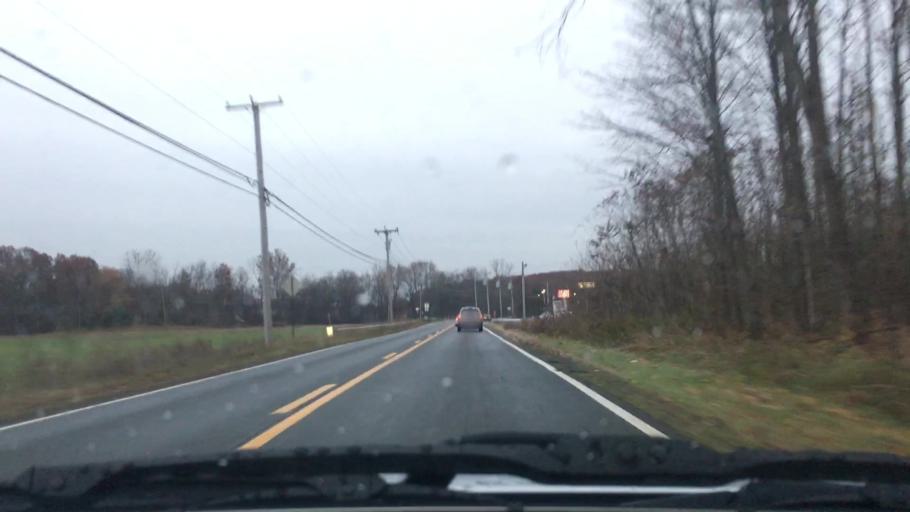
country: US
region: Massachusetts
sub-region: Hampden County
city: Southwick
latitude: 42.0737
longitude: -72.7671
